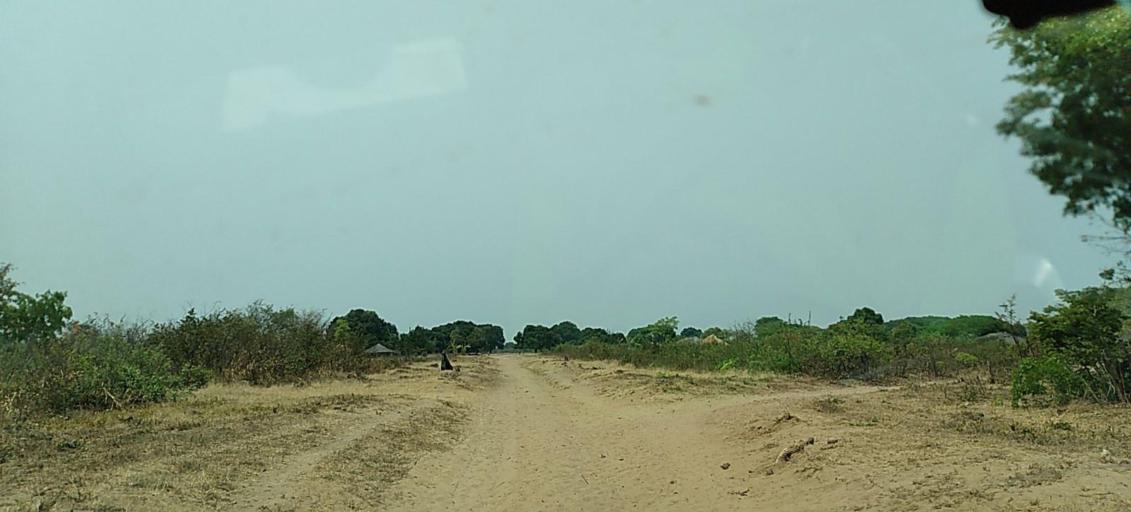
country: ZM
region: Western
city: Lukulu
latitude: -14.1546
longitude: 23.3035
